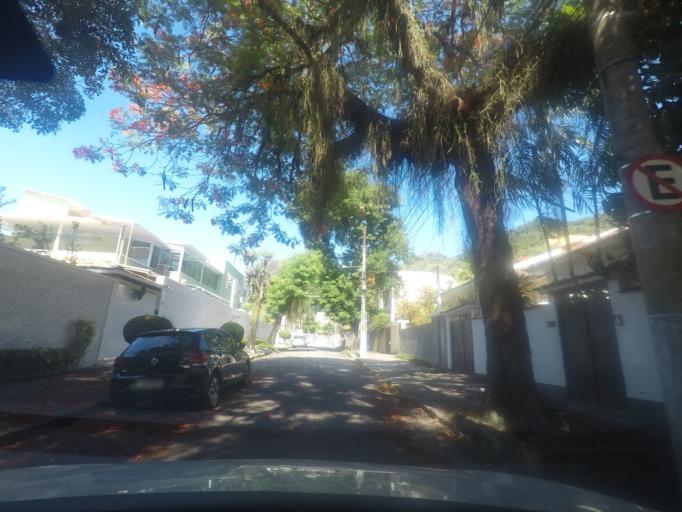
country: BR
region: Rio de Janeiro
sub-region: Niteroi
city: Niteroi
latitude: -22.9210
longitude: -43.0889
